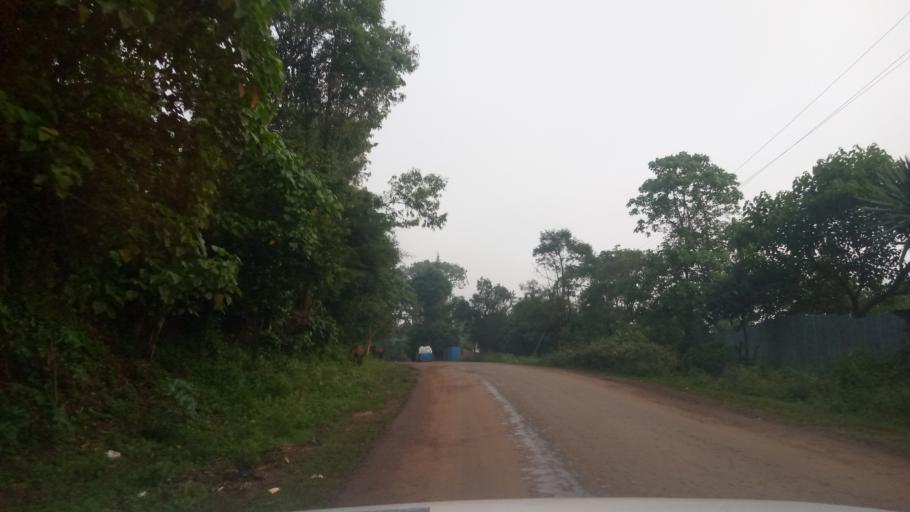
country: ET
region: Oromiya
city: Jima
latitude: 7.6914
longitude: 36.8248
